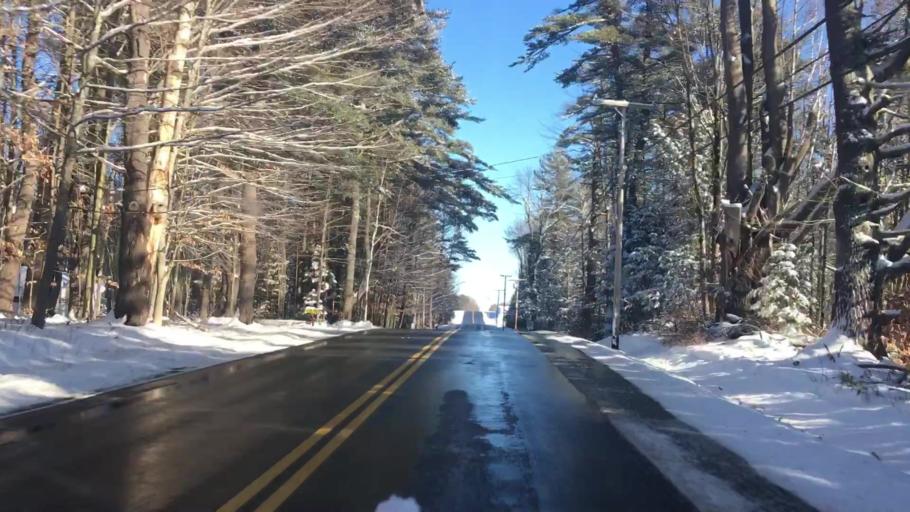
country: US
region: Maine
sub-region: Androscoggin County
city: Lisbon Falls
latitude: 43.9487
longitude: -70.1119
